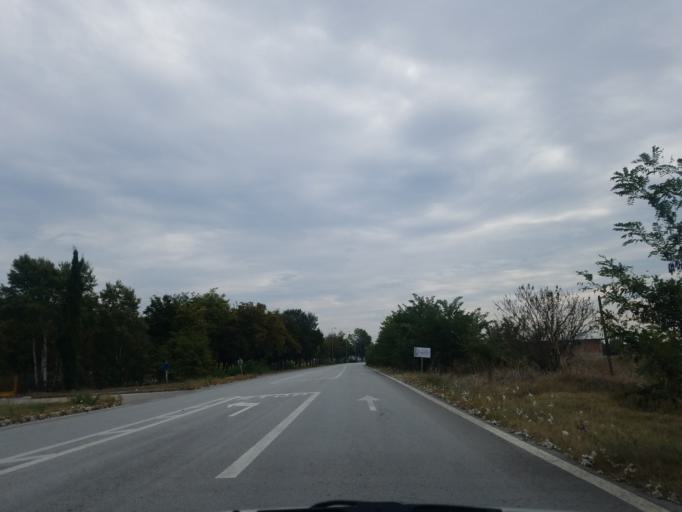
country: GR
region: Thessaly
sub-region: Nomos Kardhitsas
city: Sofades
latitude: 39.3232
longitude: 22.1066
